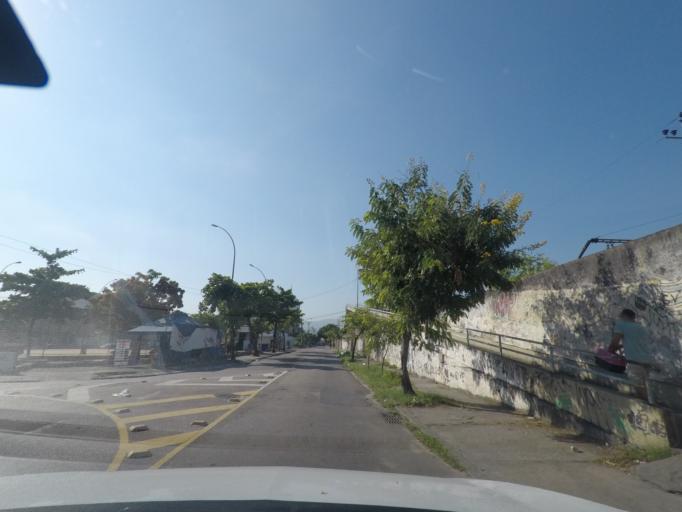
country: BR
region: Rio de Janeiro
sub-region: Rio De Janeiro
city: Rio de Janeiro
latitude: -22.8621
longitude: -43.2570
